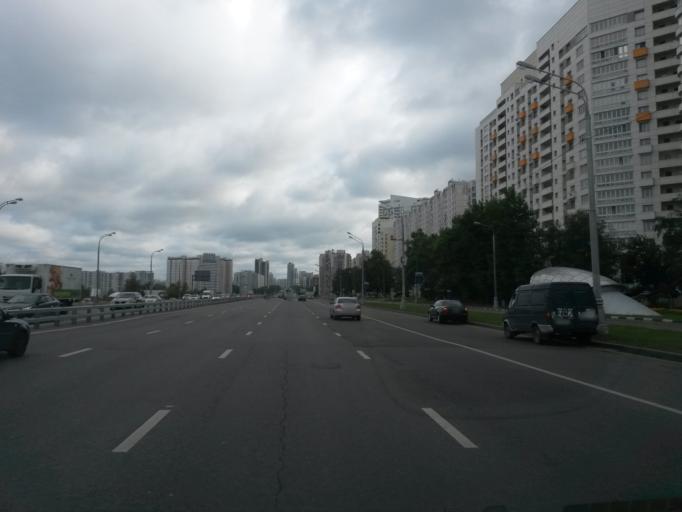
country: RU
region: Moscow
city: Troparevo
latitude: 55.6445
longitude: 37.4717
